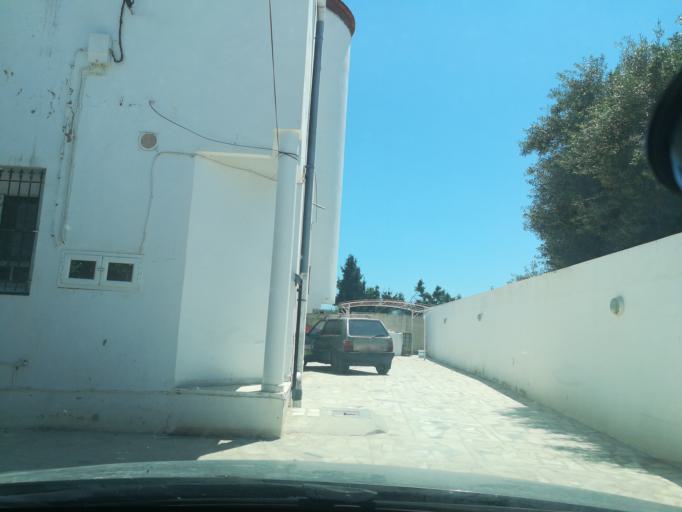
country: TN
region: Safaqis
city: Al Qarmadah
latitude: 34.8118
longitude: 10.7499
